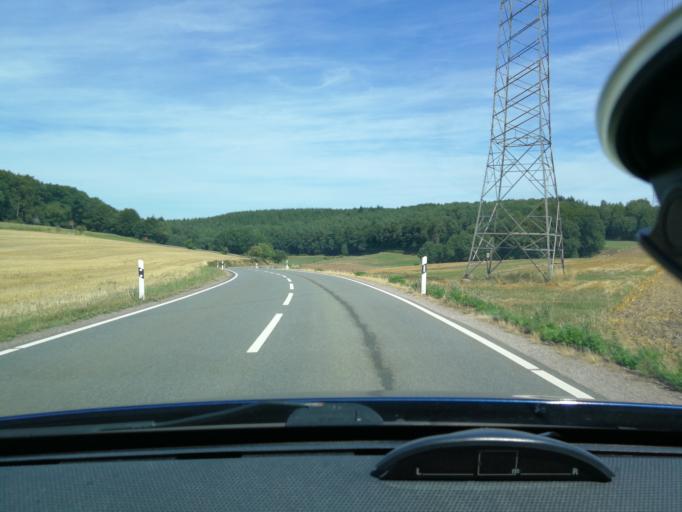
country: DE
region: Rheinland-Pfalz
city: Heidweiler
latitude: 49.9171
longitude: 6.7519
